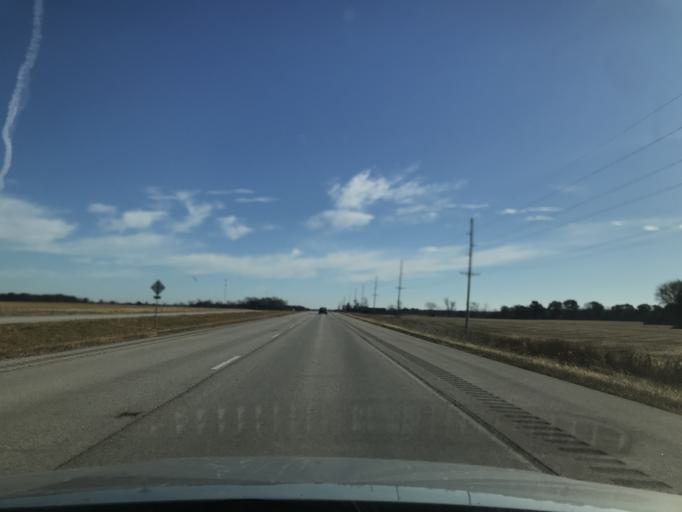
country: US
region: Illinois
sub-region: Hancock County
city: Carthage
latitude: 40.4149
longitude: -91.0506
